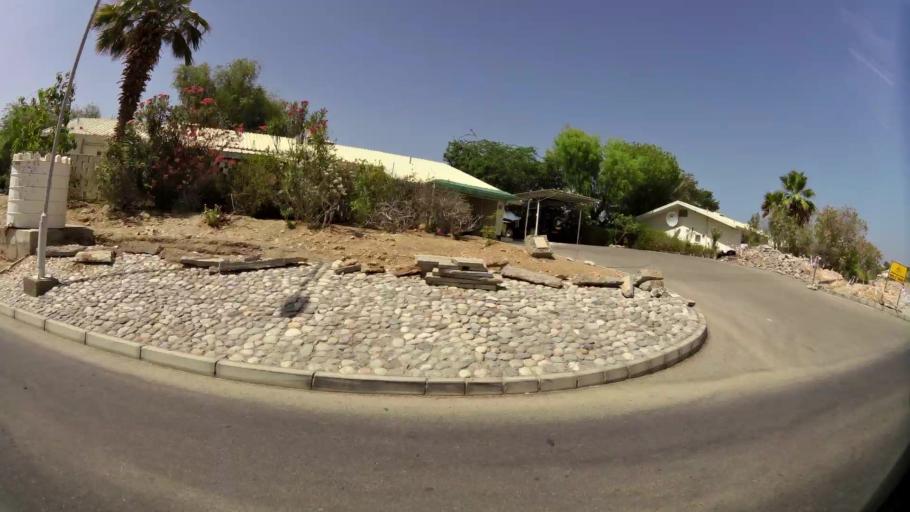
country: OM
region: Muhafazat Masqat
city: Muscat
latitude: 23.6354
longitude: 58.4907
